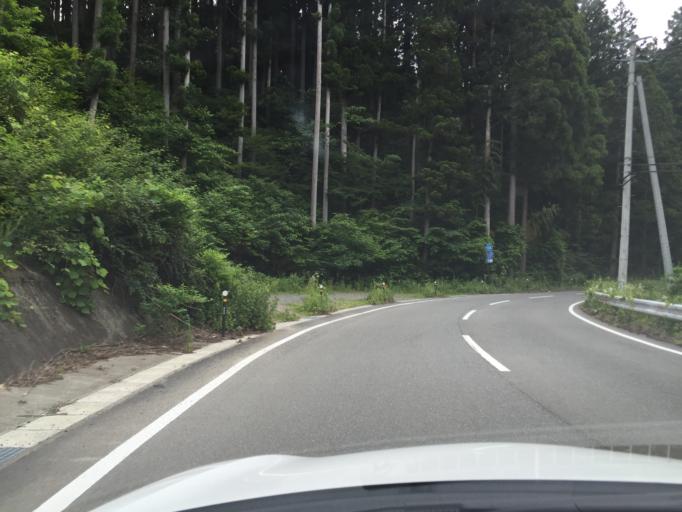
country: JP
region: Fukushima
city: Iwaki
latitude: 37.1402
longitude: 140.6987
